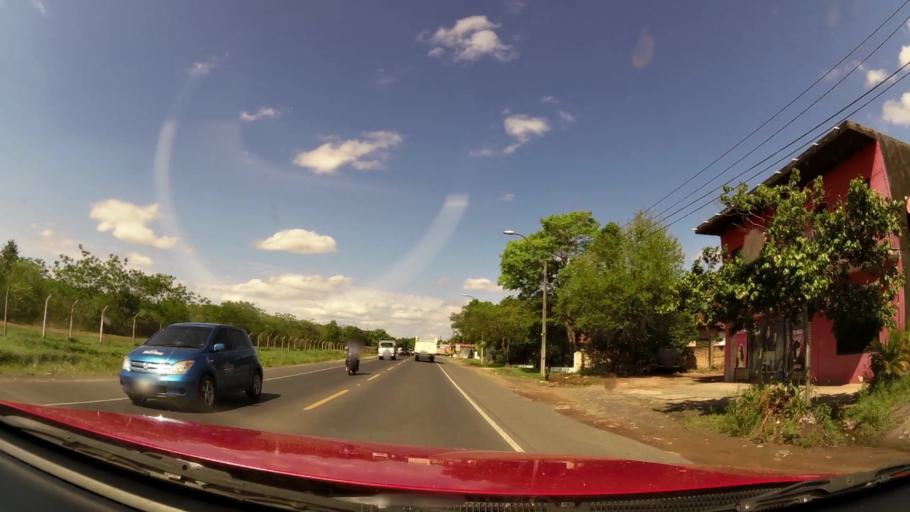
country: PY
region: Central
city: Fernando de la Mora
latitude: -25.2803
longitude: -57.5319
